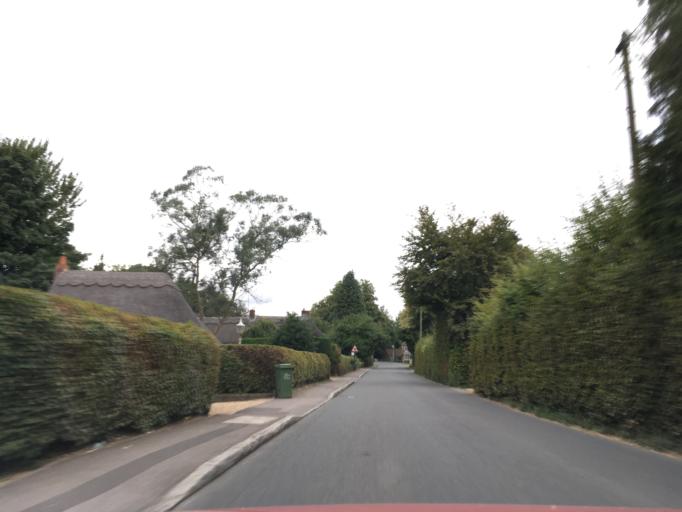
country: GB
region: England
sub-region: Wiltshire
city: Bremhill
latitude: 51.4115
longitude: -2.0515
